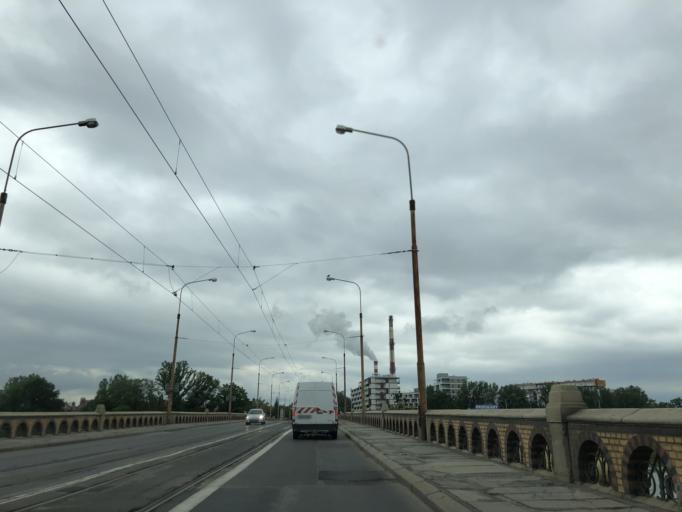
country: PL
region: Lower Silesian Voivodeship
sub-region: Powiat wroclawski
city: Wroclaw
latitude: 51.1325
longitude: 17.0280
